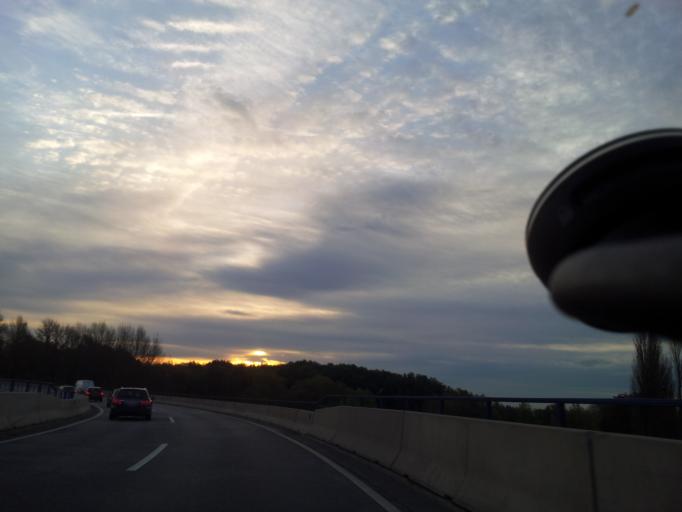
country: DE
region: Lower Saxony
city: Leiferde
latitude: 52.2311
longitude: 10.5088
